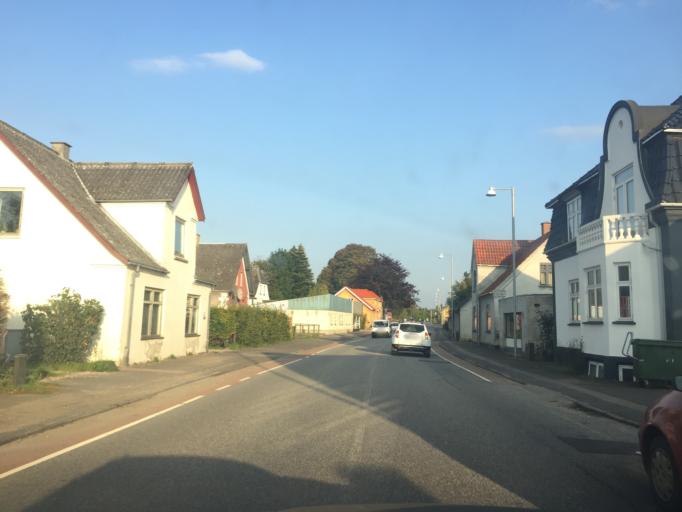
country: DK
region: Zealand
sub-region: Kalundborg Kommune
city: Hong
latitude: 55.5416
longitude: 11.3778
